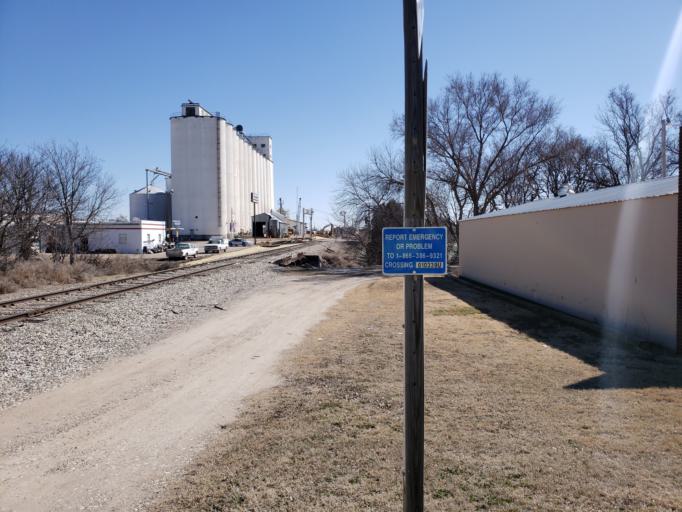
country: US
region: Kansas
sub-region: Ness County
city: Ness City
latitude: 38.4516
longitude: -99.9064
